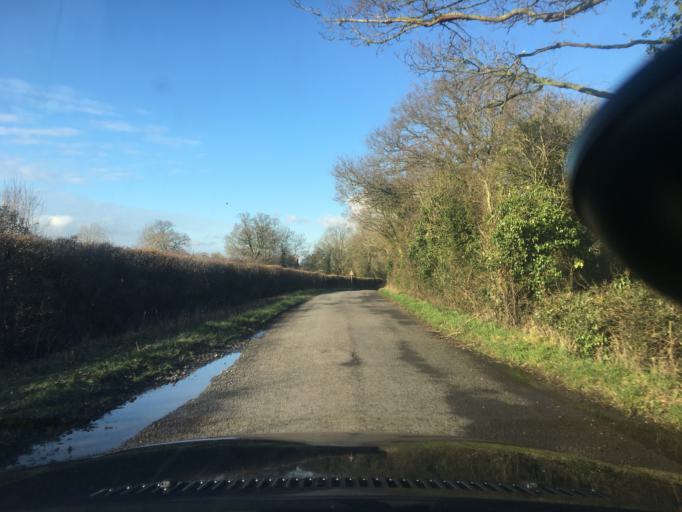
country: GB
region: England
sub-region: West Berkshire
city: Stratfield Mortimer
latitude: 51.3912
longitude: -1.0210
